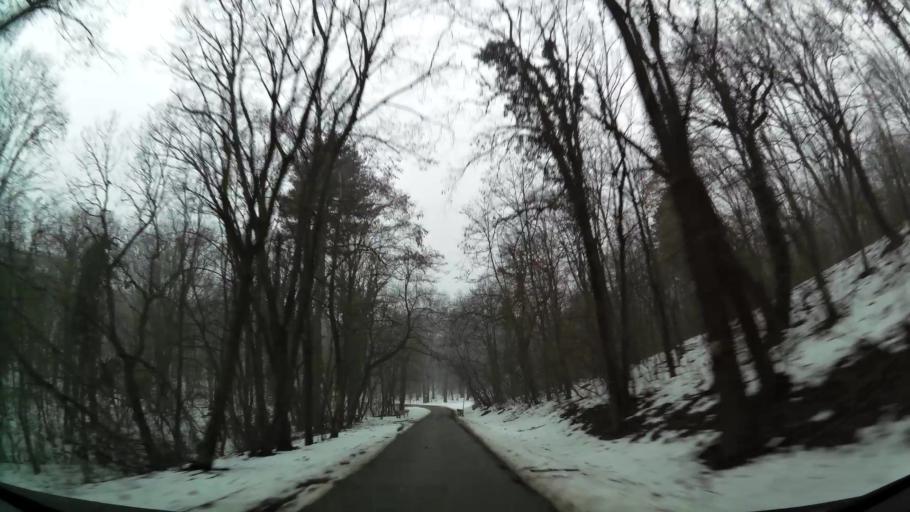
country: RS
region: Central Serbia
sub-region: Belgrade
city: Cukarica
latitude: 44.7759
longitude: 20.4302
